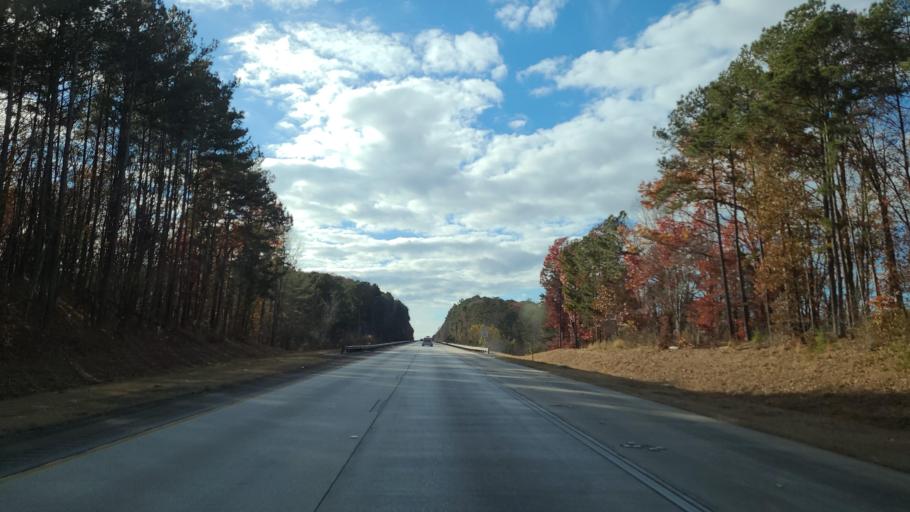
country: US
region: Georgia
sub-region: Haralson County
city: Tallapoosa
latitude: 33.6833
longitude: -85.2814
